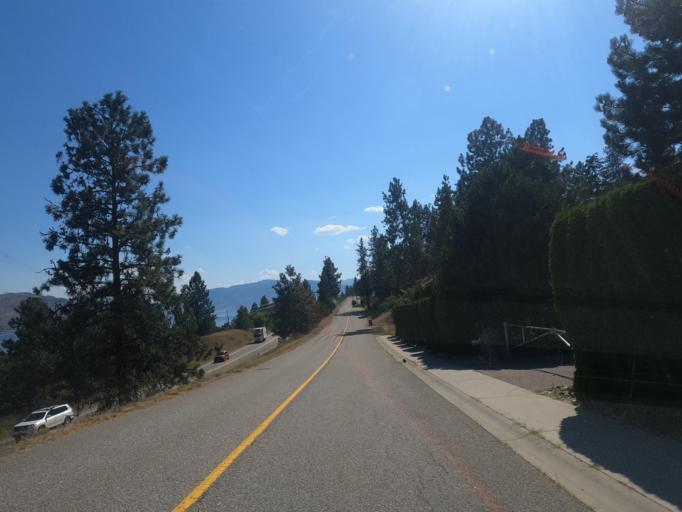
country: CA
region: British Columbia
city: Peachland
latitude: 49.7917
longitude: -119.7063
